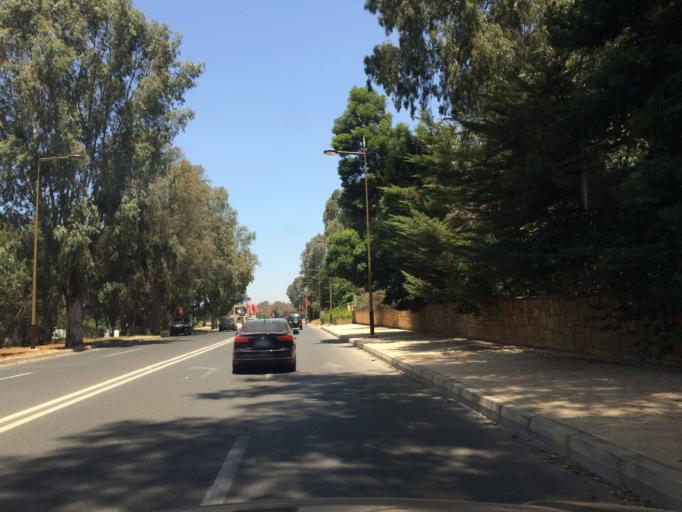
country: MA
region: Rabat-Sale-Zemmour-Zaer
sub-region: Rabat
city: Rabat
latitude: 33.9332
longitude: -6.8208
